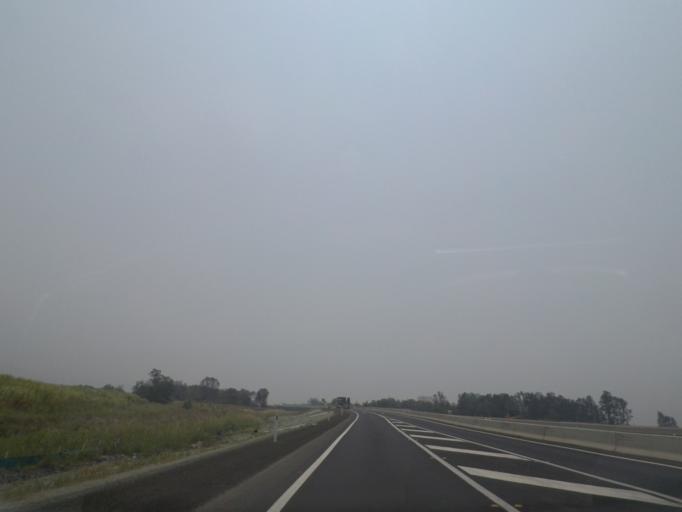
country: AU
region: New South Wales
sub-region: Clarence Valley
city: Maclean
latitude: -29.4071
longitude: 153.2425
